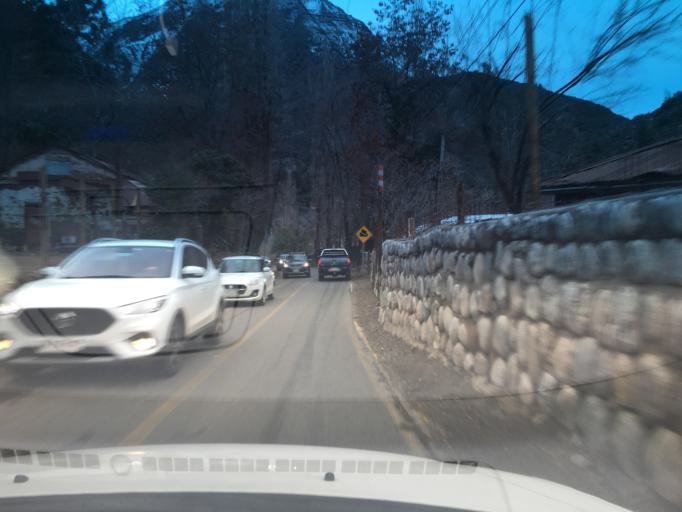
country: CL
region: Santiago Metropolitan
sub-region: Provincia de Cordillera
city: Puente Alto
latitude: -33.7330
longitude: -70.3060
